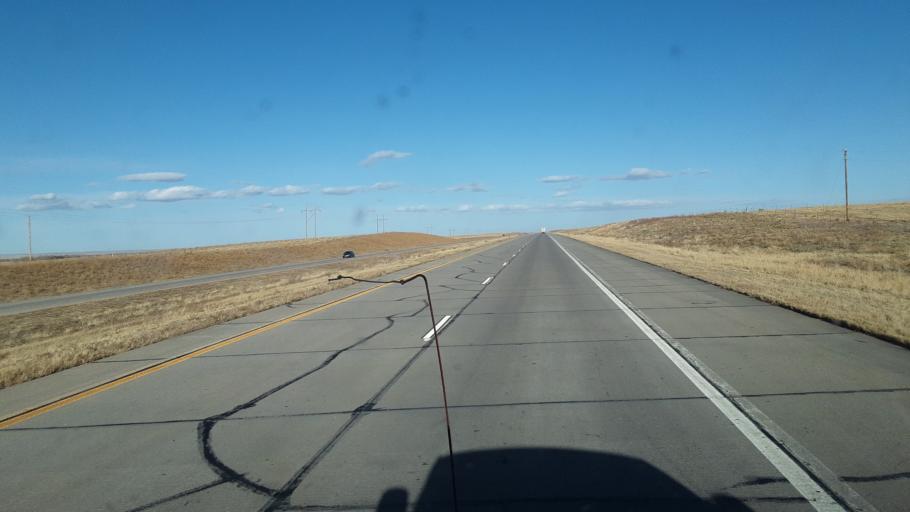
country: US
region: Colorado
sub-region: Logan County
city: Sterling
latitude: 40.6776
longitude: -103.1085
